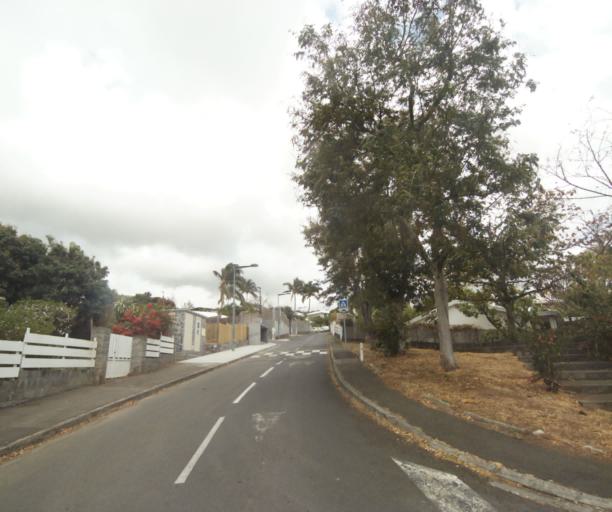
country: RE
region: Reunion
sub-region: Reunion
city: Saint-Paul
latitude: -21.0277
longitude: 55.2727
